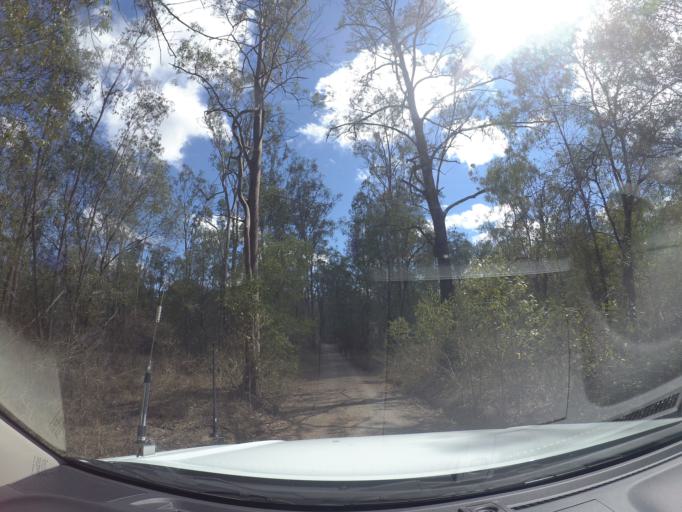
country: AU
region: Queensland
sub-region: Logan
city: North Maclean
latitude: -27.8335
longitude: 152.9670
